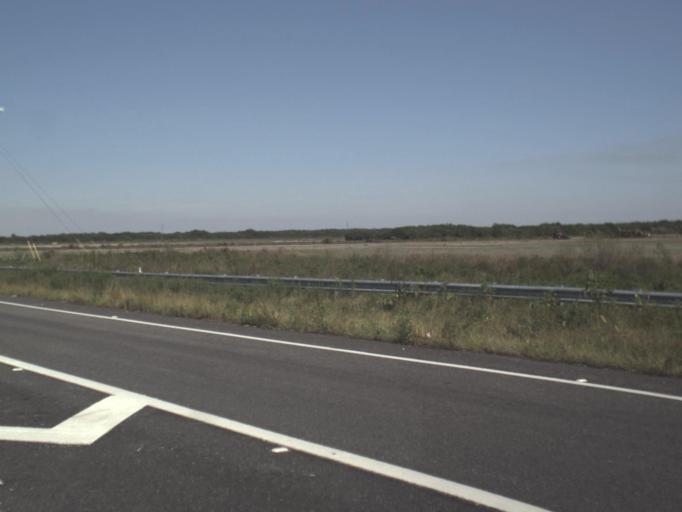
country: US
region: Florida
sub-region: Glades County
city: Moore Haven
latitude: 26.7614
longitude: -81.0829
